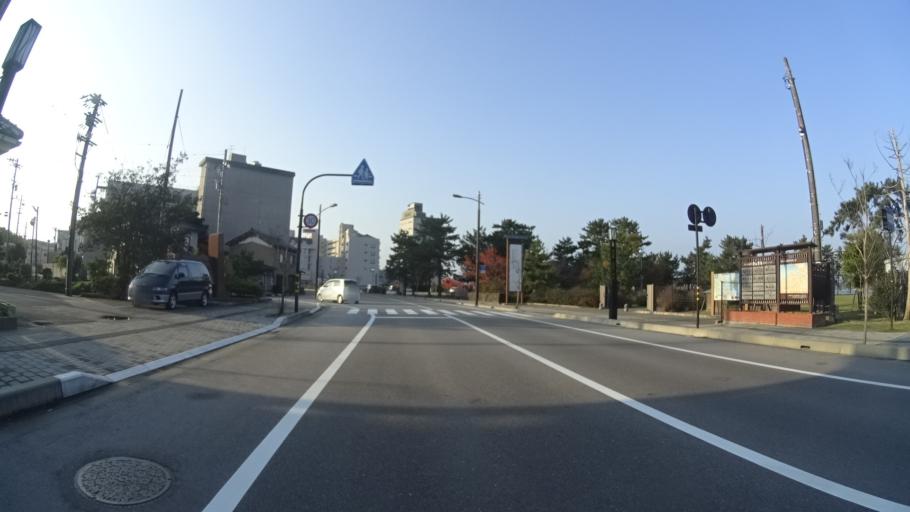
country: JP
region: Ishikawa
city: Nanao
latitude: 37.0868
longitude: 136.9237
